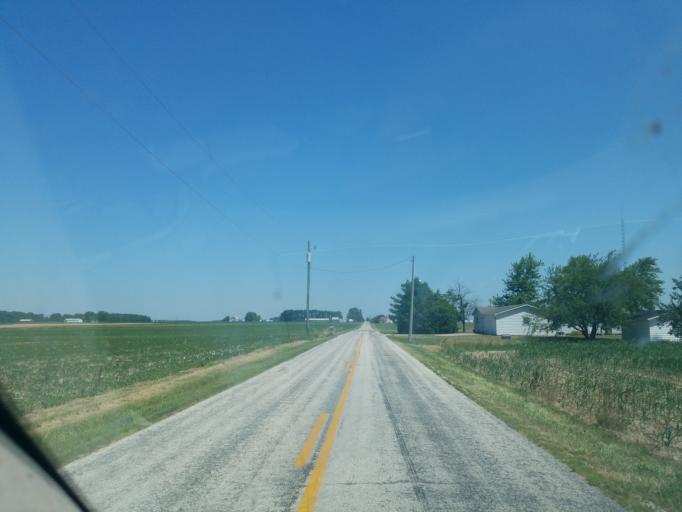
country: US
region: Ohio
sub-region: Mercer County
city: Rockford
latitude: 40.5884
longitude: -84.7084
